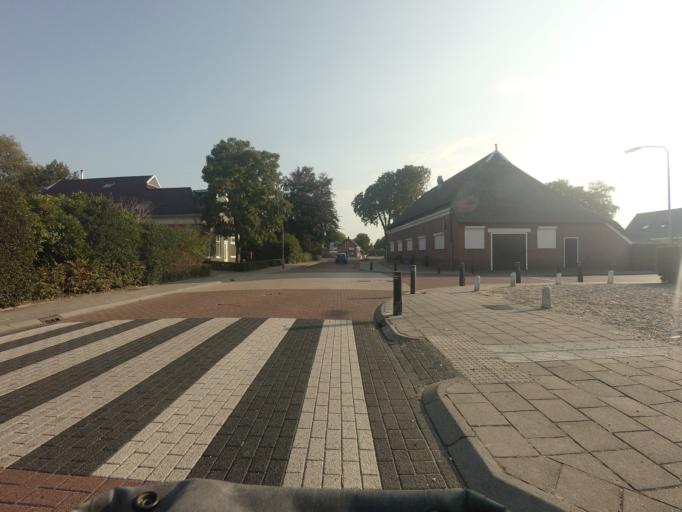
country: NL
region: Groningen
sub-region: Gemeente Haren
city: Haren
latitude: 53.1360
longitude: 6.5640
